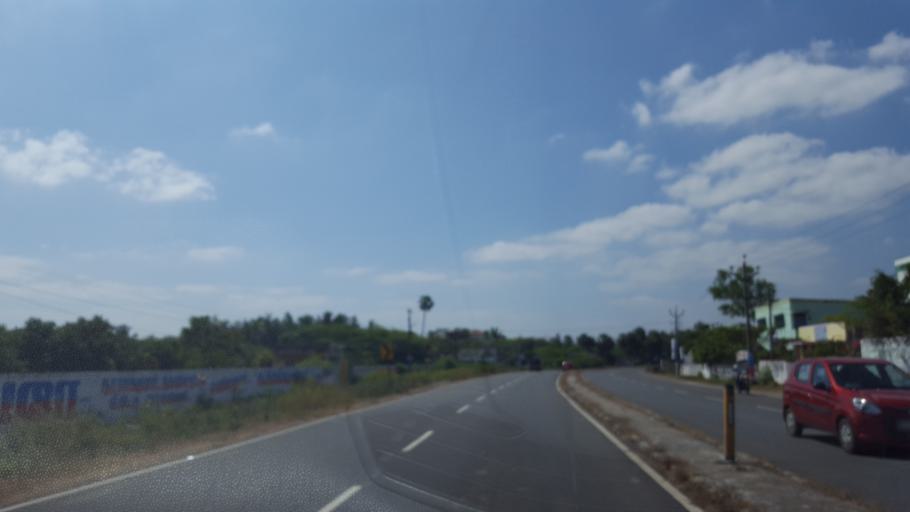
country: IN
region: Tamil Nadu
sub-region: Kancheepuram
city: Mamallapuram
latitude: 12.6446
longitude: 80.1744
